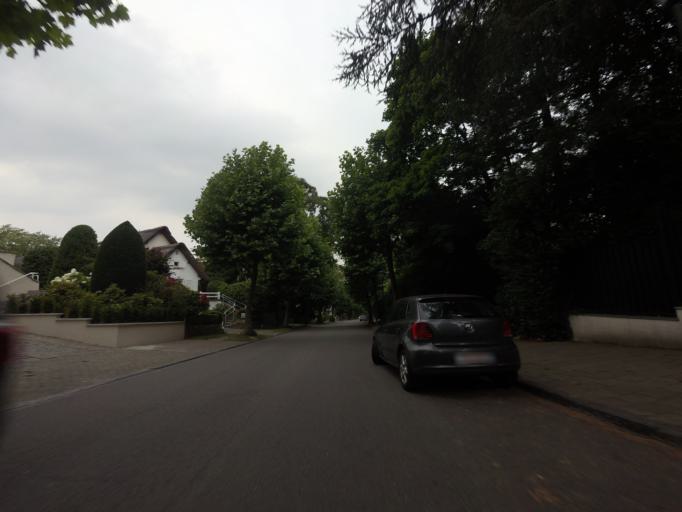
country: BE
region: Flanders
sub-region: Provincie Vlaams-Brabant
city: Linkebeek
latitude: 50.7986
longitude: 4.3549
